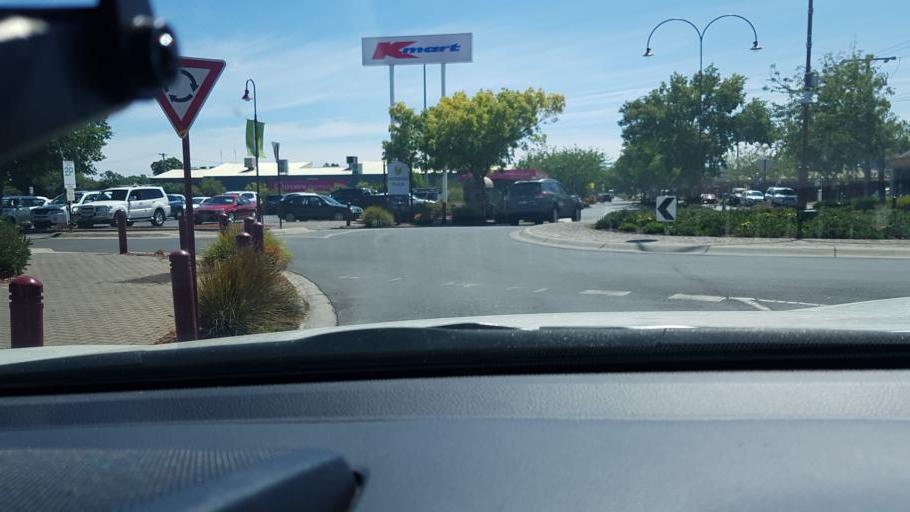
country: AU
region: Victoria
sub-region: Horsham
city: Horsham
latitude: -36.7156
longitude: 142.1971
